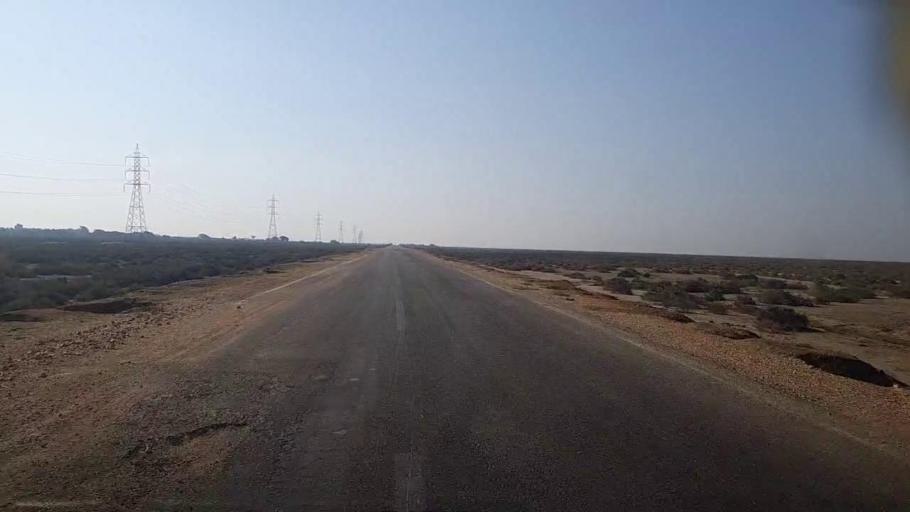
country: PK
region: Sindh
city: Gharo
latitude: 24.6263
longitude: 67.4969
